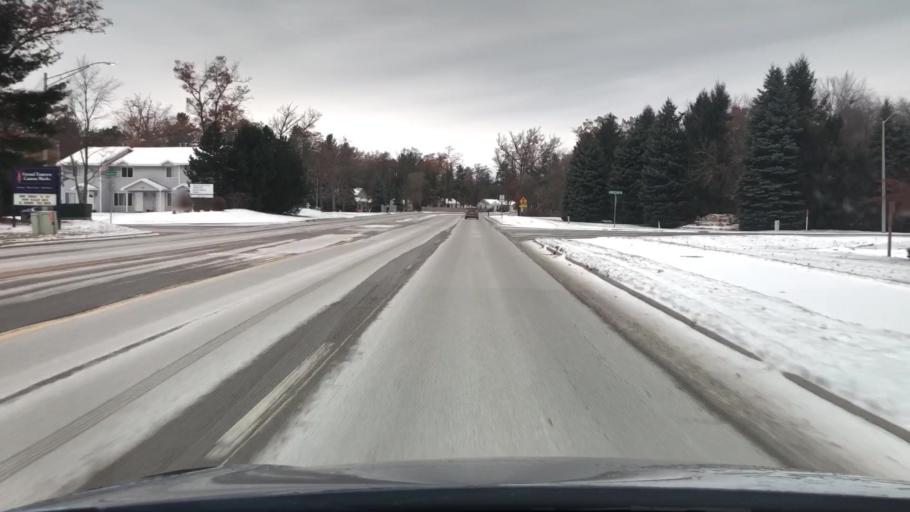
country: US
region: Michigan
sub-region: Grand Traverse County
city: Traverse City
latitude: 44.7427
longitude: -85.5605
